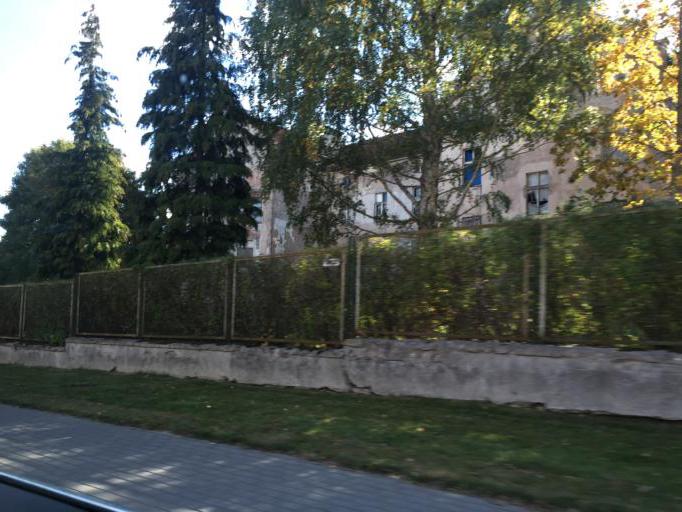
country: PL
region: Warmian-Masurian Voivodeship
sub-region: Powiat bartoszycki
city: Bartoszyce
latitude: 54.2462
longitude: 20.8130
